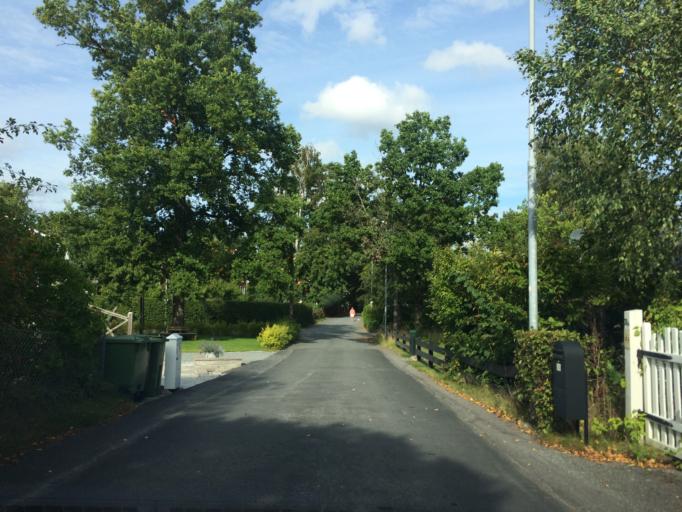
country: SE
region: Stockholm
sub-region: Sollentuna Kommun
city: Sollentuna
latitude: 59.4604
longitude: 17.9277
